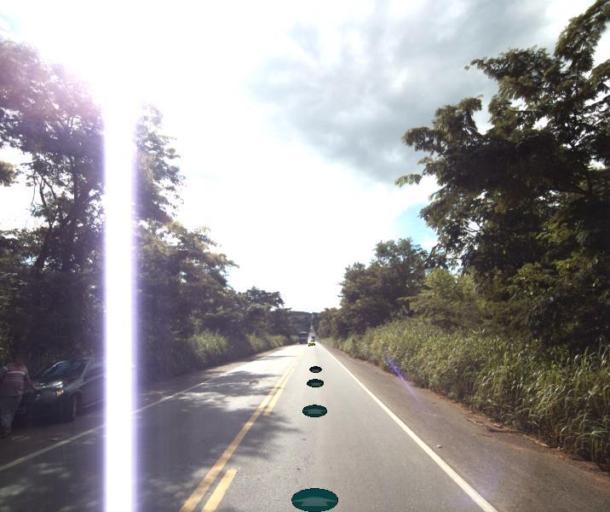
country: BR
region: Goias
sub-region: Jaragua
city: Jaragua
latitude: -15.6796
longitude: -49.3429
